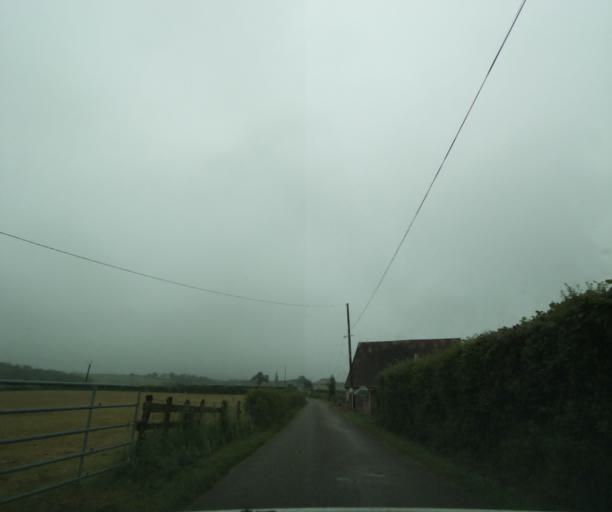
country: FR
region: Bourgogne
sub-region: Departement de Saone-et-Loire
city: Charolles
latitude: 46.4186
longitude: 4.3785
